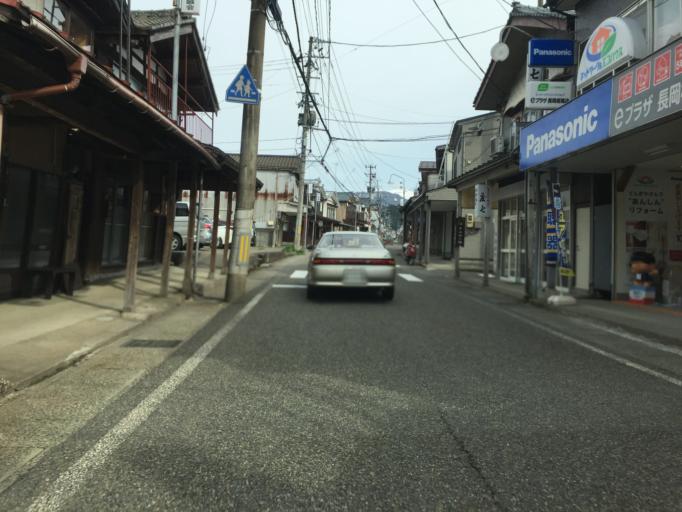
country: JP
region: Niigata
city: Tochio-honcho
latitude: 37.4723
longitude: 138.9992
